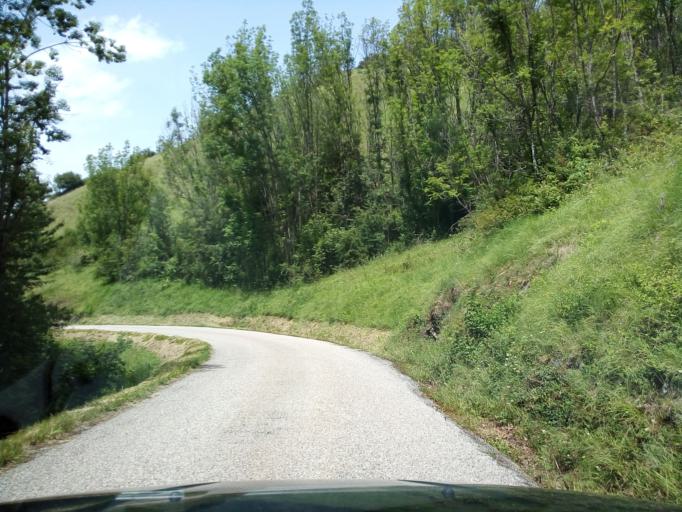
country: FR
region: Rhone-Alpes
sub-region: Departement de l'Isere
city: Poisat
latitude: 45.1524
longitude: 5.7773
